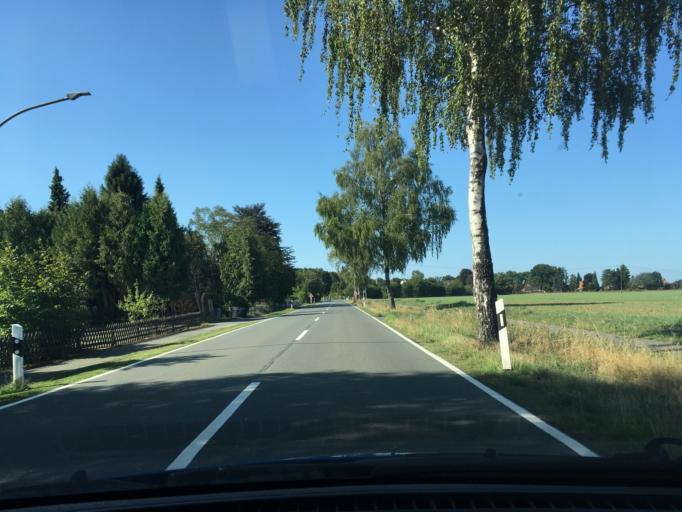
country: DE
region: Lower Saxony
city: Wriedel
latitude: 53.0046
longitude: 10.2659
